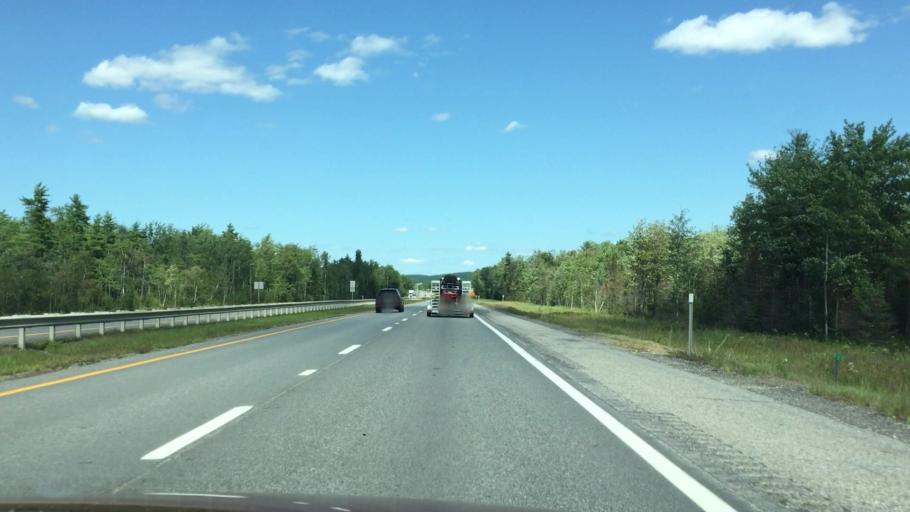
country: US
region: Maine
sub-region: Androscoggin County
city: Sabattus
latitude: 44.0929
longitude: -70.0982
